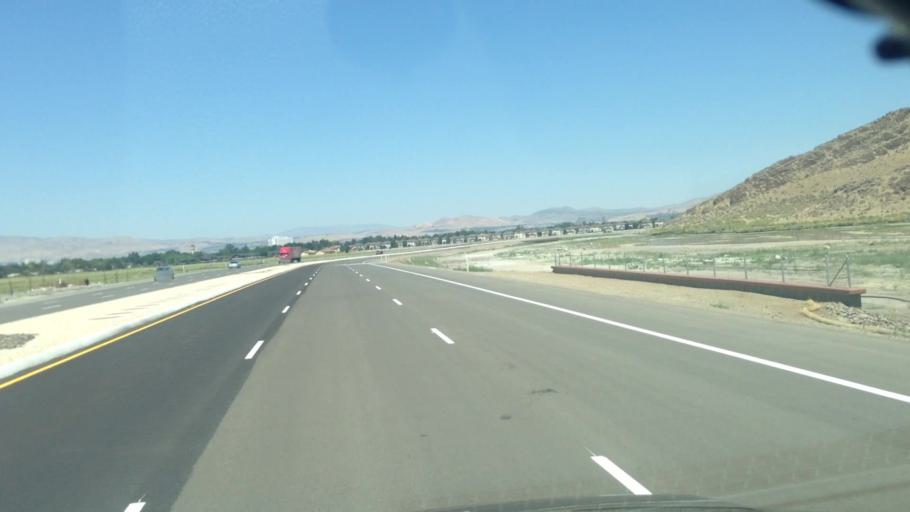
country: US
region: Nevada
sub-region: Washoe County
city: Sparks
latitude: 39.4736
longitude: -119.7356
